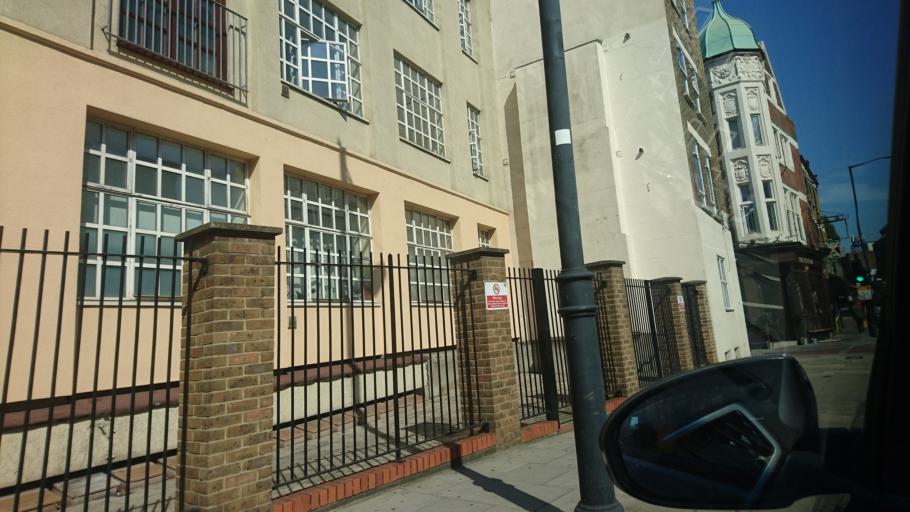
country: GB
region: England
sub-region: Greater London
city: Hackney
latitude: 51.5482
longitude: -0.0481
